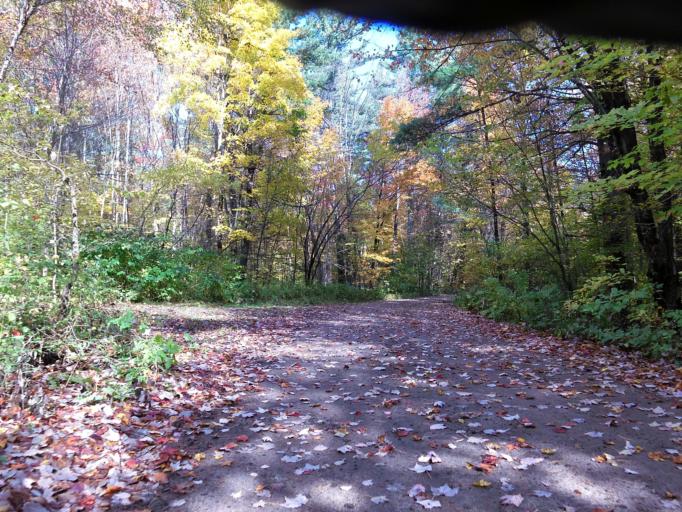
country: CA
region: Ontario
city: Petawawa
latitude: 45.8077
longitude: -77.2800
